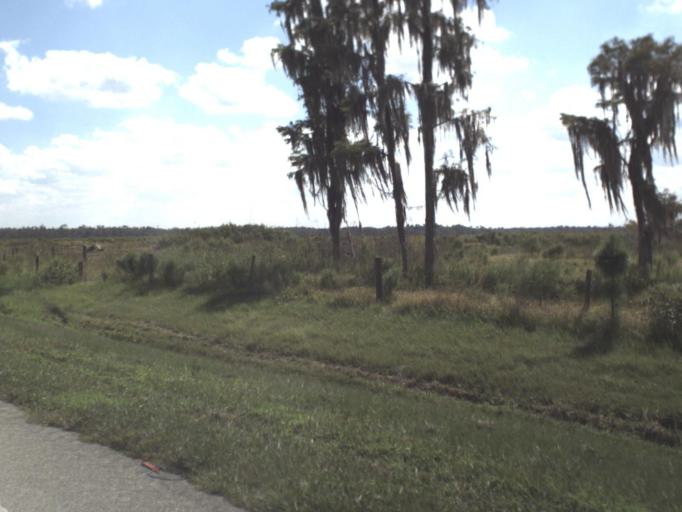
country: US
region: Florida
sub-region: Highlands County
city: Sebring
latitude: 27.4431
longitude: -81.6174
